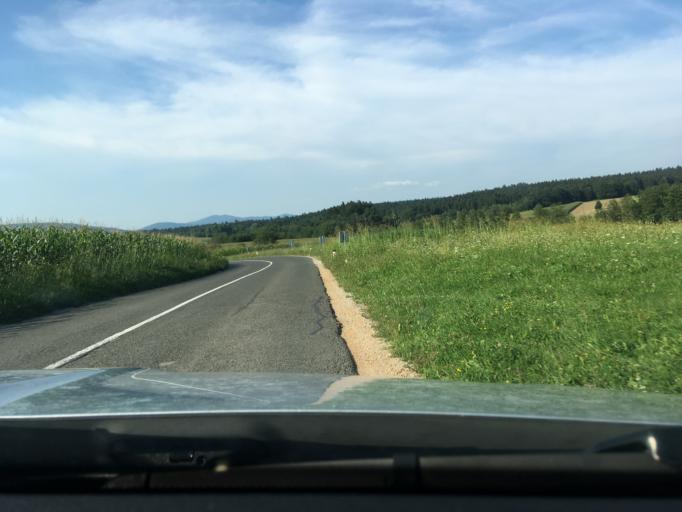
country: SI
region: Crnomelj
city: Crnomelj
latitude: 45.5349
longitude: 15.1634
